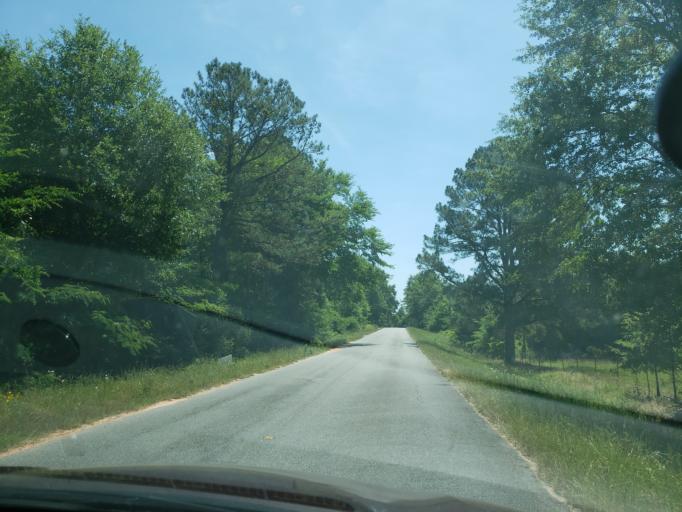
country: US
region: Alabama
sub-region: Elmore County
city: Tallassee
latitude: 32.5841
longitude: -85.8575
